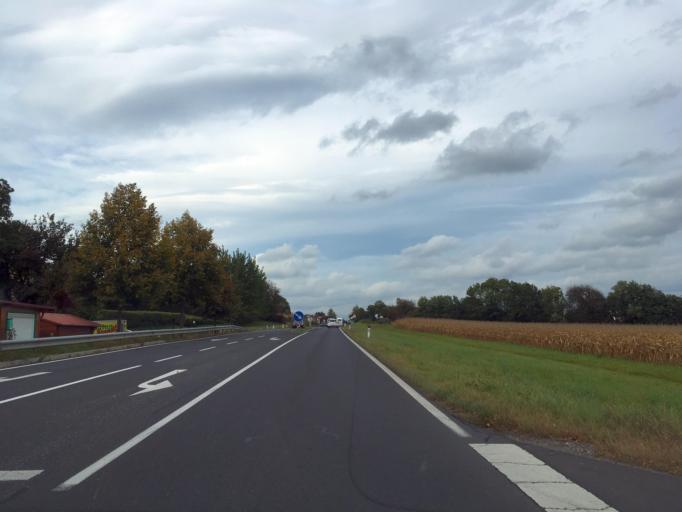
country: AT
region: Styria
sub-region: Politischer Bezirk Hartberg-Fuerstenfeld
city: Hartberg
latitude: 47.2912
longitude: 15.9793
